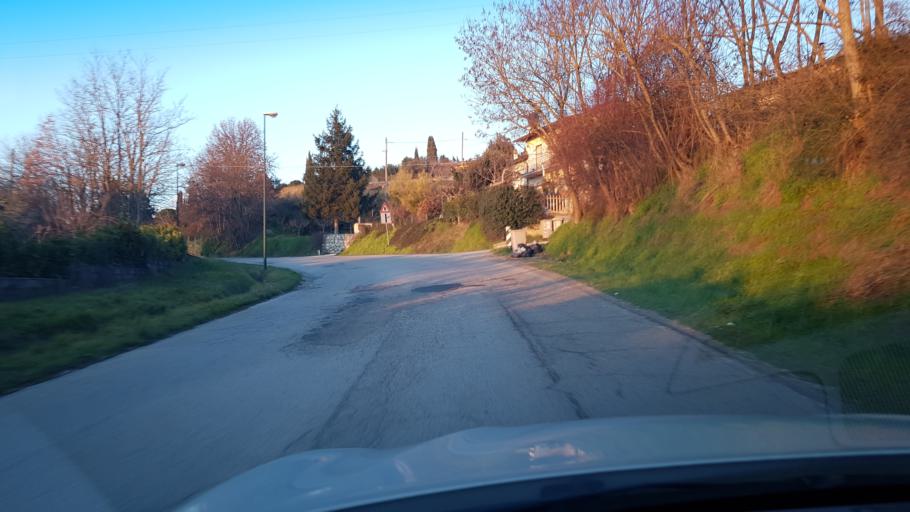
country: IT
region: Umbria
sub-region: Provincia di Perugia
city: Torgiano
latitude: 43.0130
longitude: 12.4358
